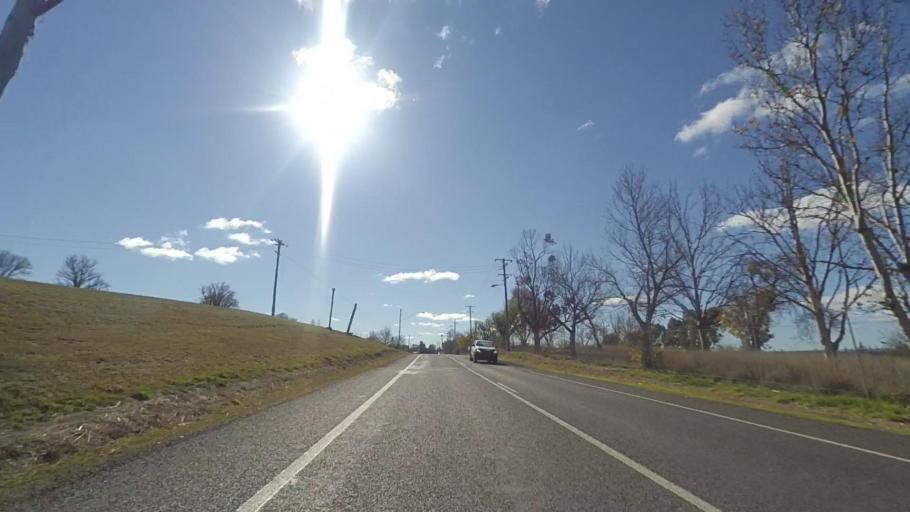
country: AU
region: New South Wales
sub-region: Bathurst Regional
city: Bathurst
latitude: -33.4432
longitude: 149.5788
